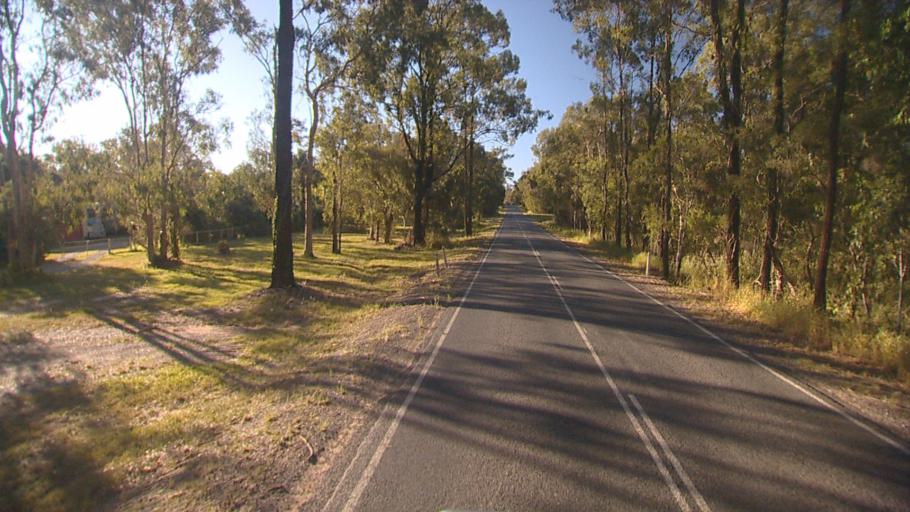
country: AU
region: Queensland
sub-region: Logan
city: Logan Reserve
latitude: -27.7299
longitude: 153.0894
